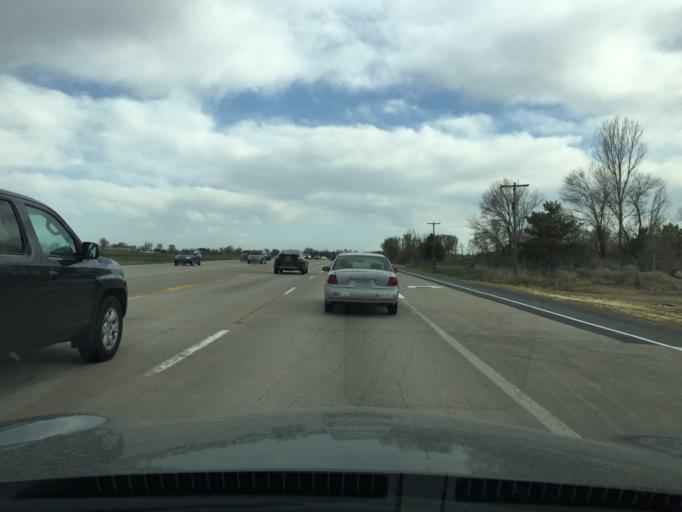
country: US
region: Colorado
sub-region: Boulder County
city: Erie
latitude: 40.0480
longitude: -105.1028
